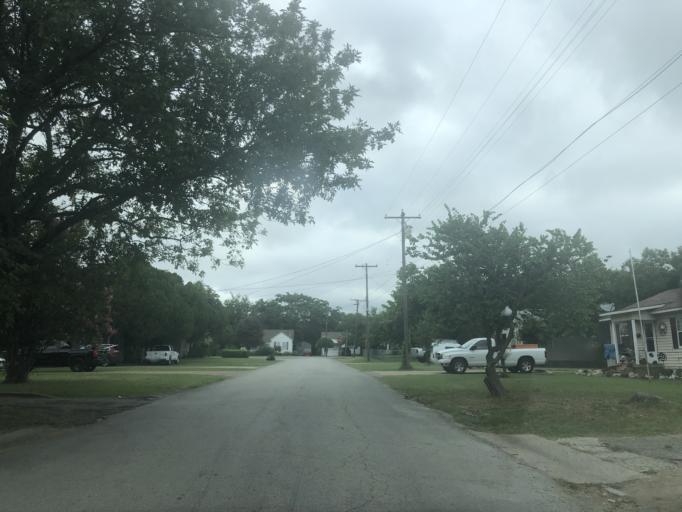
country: US
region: Texas
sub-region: Dallas County
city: Duncanville
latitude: 32.6564
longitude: -96.9066
